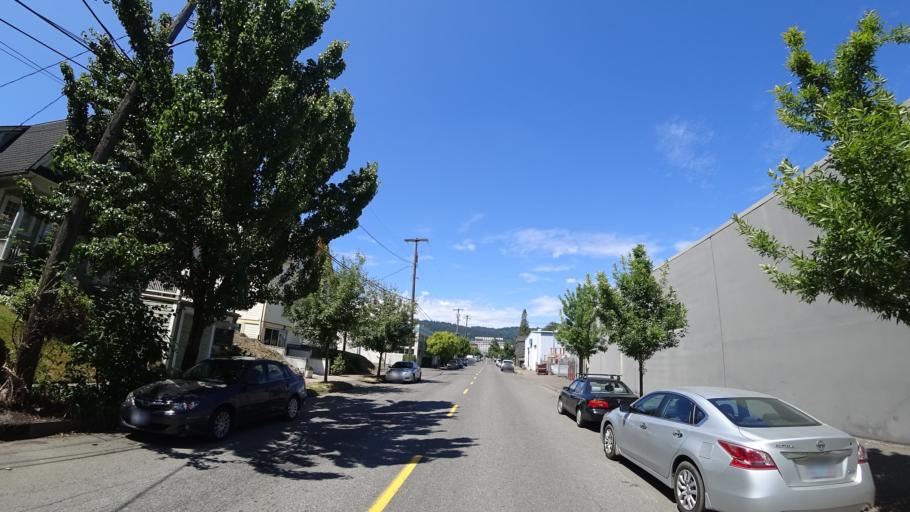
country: US
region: Oregon
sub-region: Multnomah County
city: Portland
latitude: 45.5377
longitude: -122.6952
